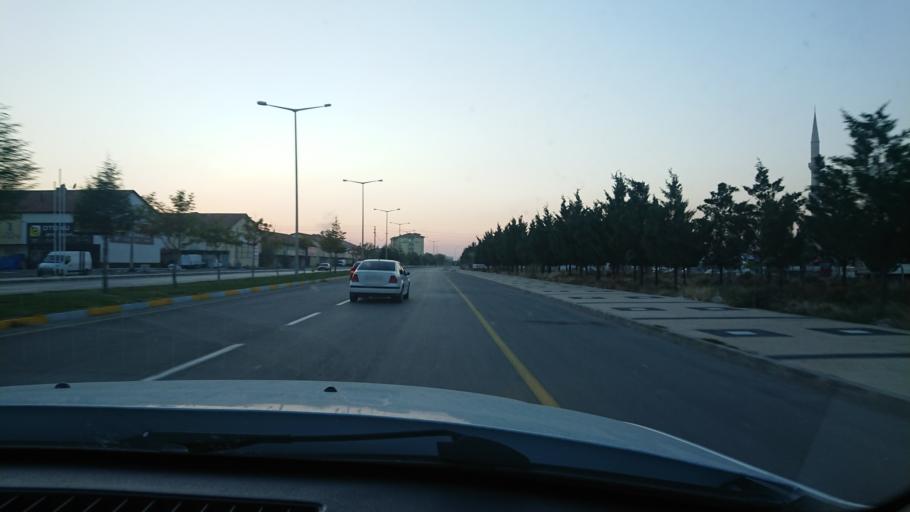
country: TR
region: Aksaray
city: Aksaray
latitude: 38.3572
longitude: 33.9869
